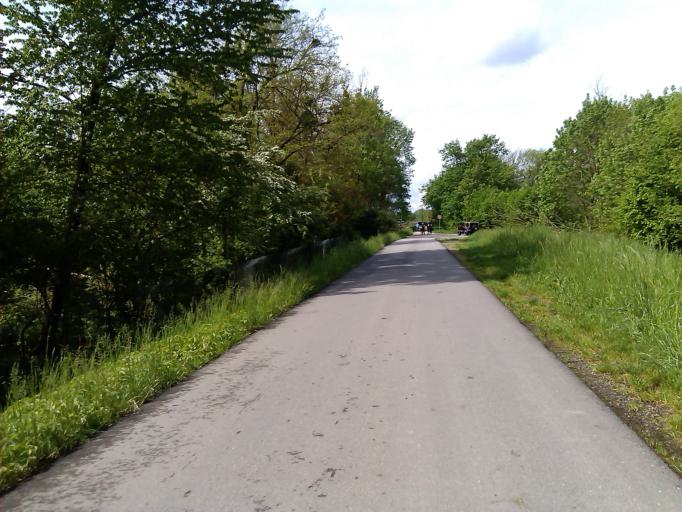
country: FR
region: Alsace
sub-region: Departement du Bas-Rhin
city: La Wantzenau
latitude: 48.6467
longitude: 7.8295
